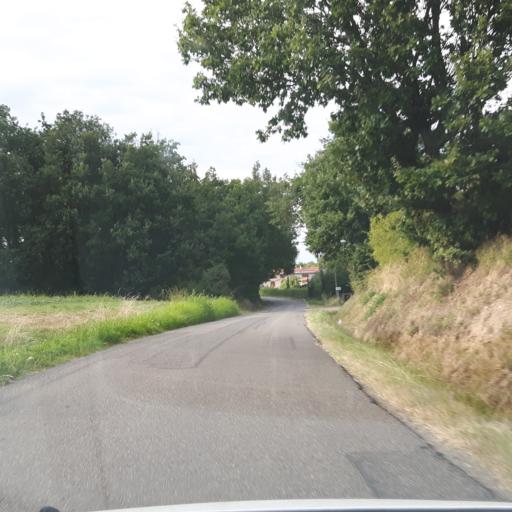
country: FR
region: Midi-Pyrenees
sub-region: Departement de la Haute-Garonne
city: Castelnau-d'Estretefonds
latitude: 43.8038
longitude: 1.3534
